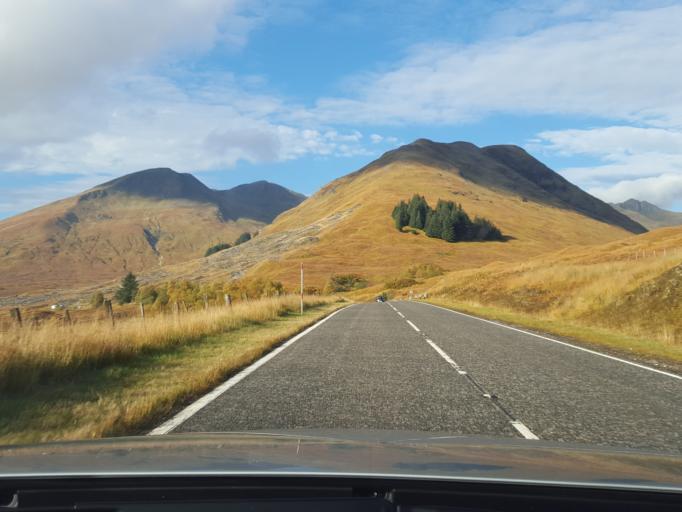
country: GB
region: Scotland
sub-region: Highland
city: Fort William
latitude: 57.1590
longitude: -5.1551
